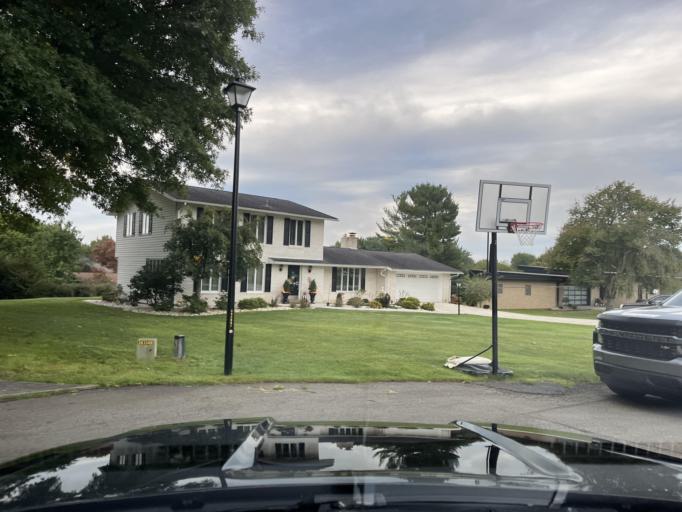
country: US
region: Pennsylvania
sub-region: Fayette County
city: Leith-Hatfield
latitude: 39.8759
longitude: -79.7237
